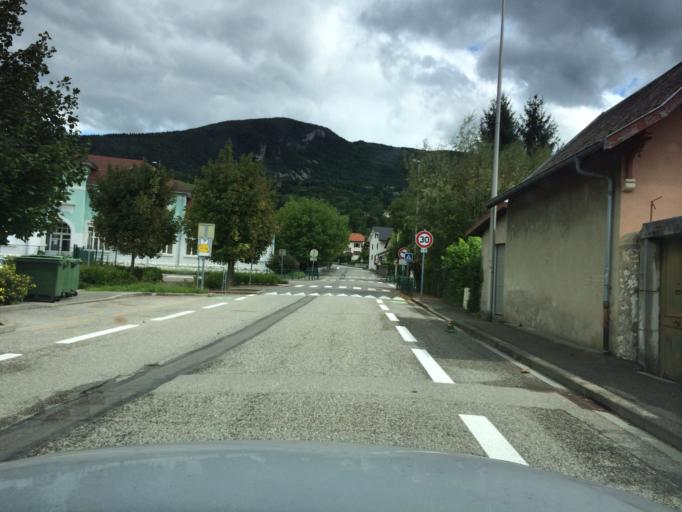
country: FR
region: Rhone-Alpes
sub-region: Departement de la Haute-Savoie
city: Versonnex
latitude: 45.9593
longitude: 5.8382
